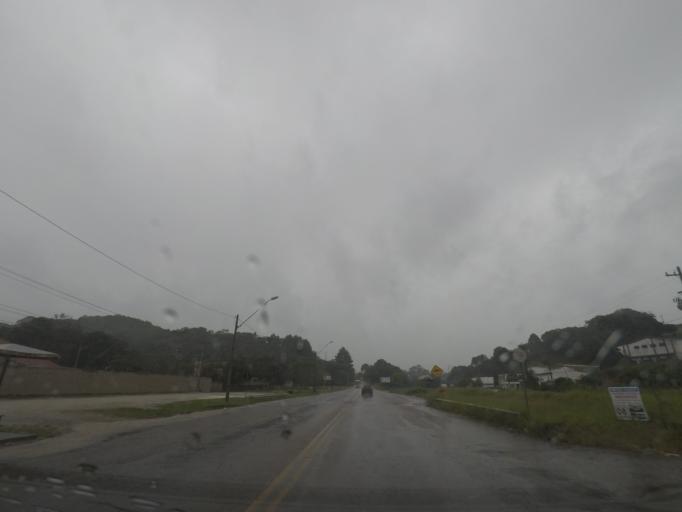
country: BR
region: Parana
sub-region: Almirante Tamandare
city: Almirante Tamandare
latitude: -25.3567
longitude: -49.2811
